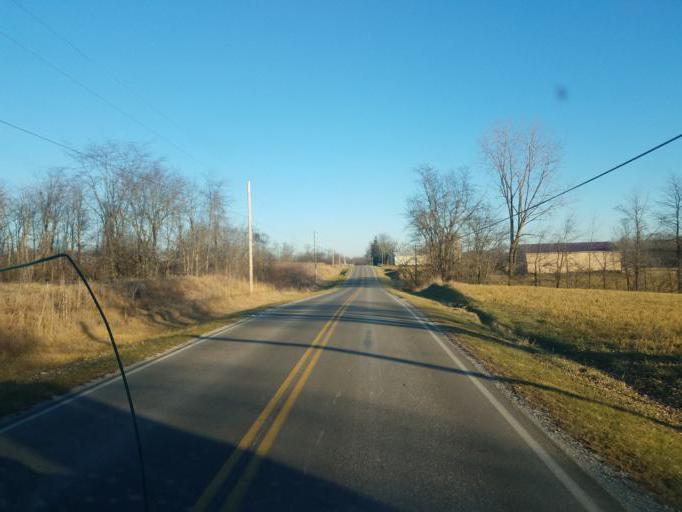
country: US
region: Ohio
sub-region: Hardin County
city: Kenton
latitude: 40.6215
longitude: -83.4835
